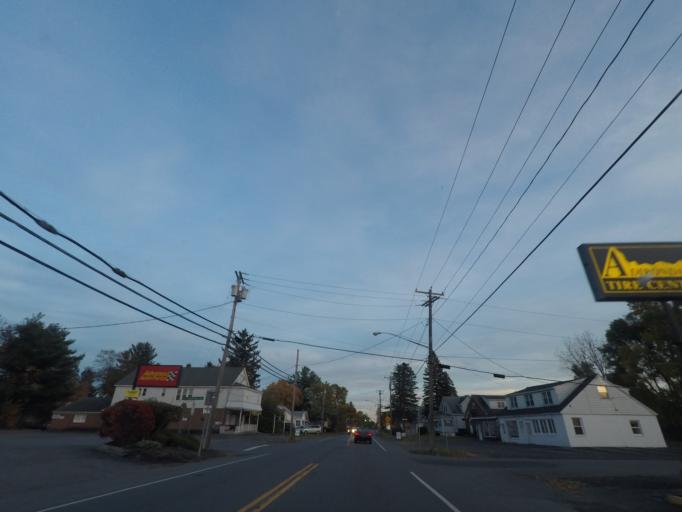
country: US
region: New York
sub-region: Schenectady County
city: Rotterdam
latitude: 42.7850
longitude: -73.9659
